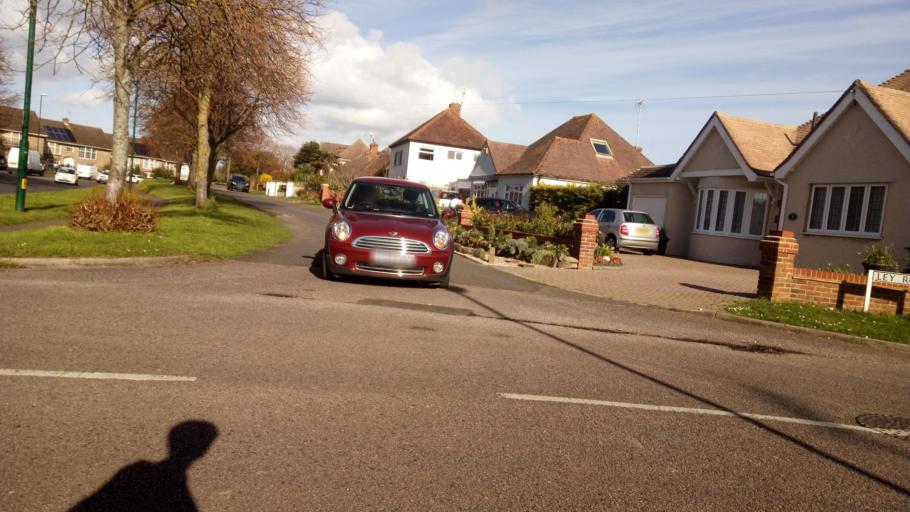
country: GB
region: England
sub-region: West Sussex
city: Bognor Regis
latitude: 50.7925
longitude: -0.6465
